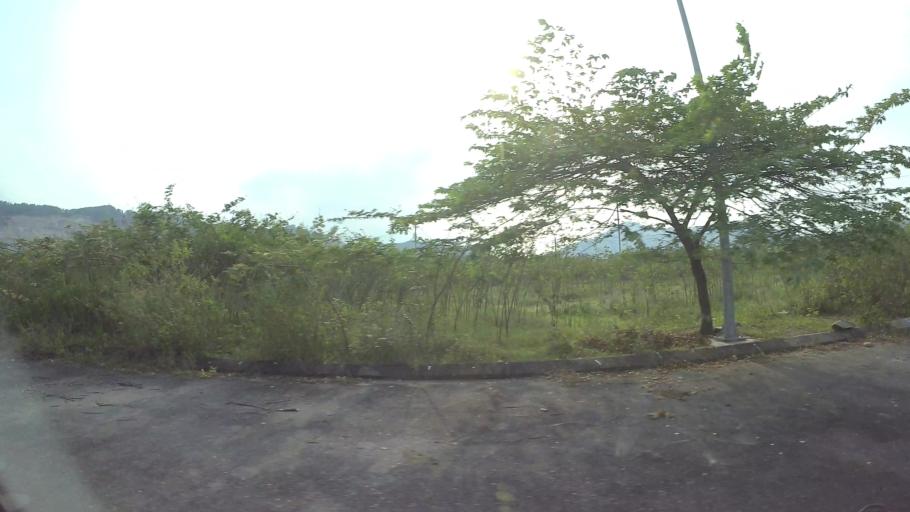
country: VN
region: Da Nang
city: Lien Chieu
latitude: 16.0461
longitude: 108.1581
